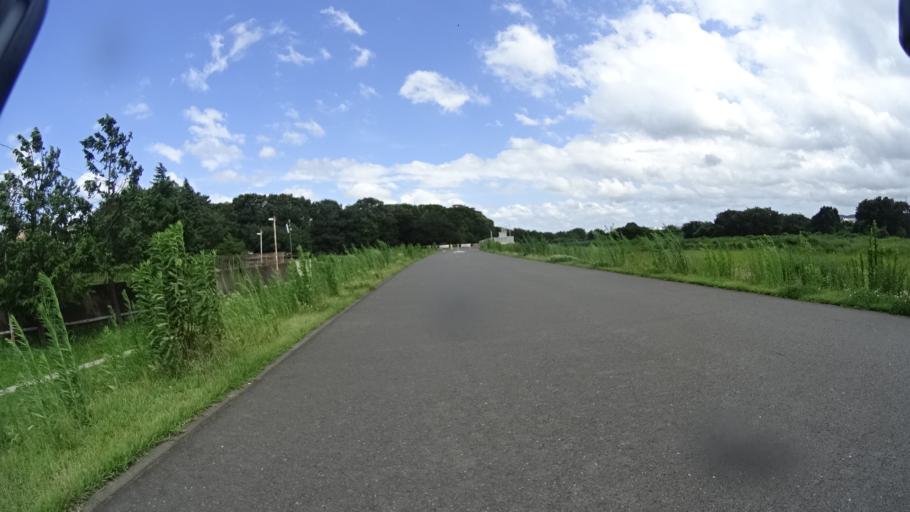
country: JP
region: Tokyo
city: Hino
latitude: 35.6831
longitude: 139.4166
